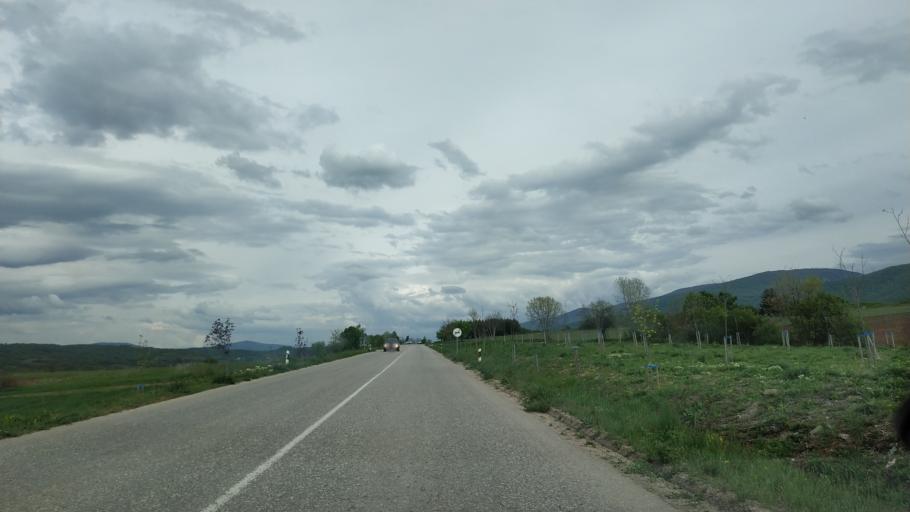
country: RS
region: Central Serbia
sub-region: Zajecarski Okrug
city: Soko Banja
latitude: 43.6556
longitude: 21.8288
